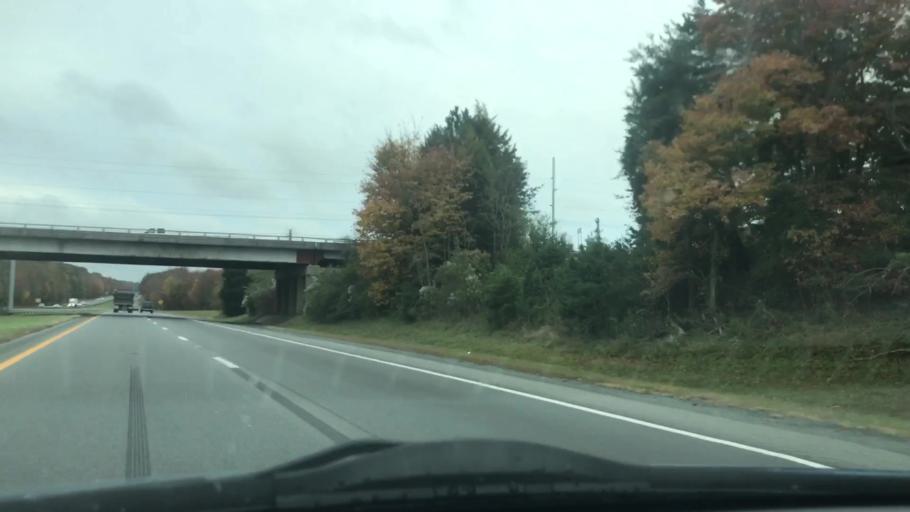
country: US
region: North Carolina
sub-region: Randolph County
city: Asheboro
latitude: 35.7536
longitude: -79.8268
